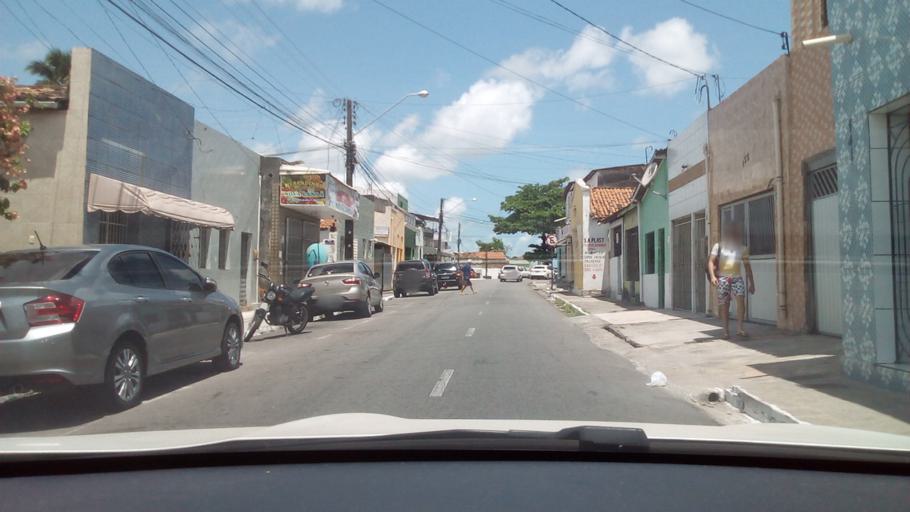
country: BR
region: Paraiba
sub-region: Joao Pessoa
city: Joao Pessoa
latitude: -7.1224
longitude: -34.8897
